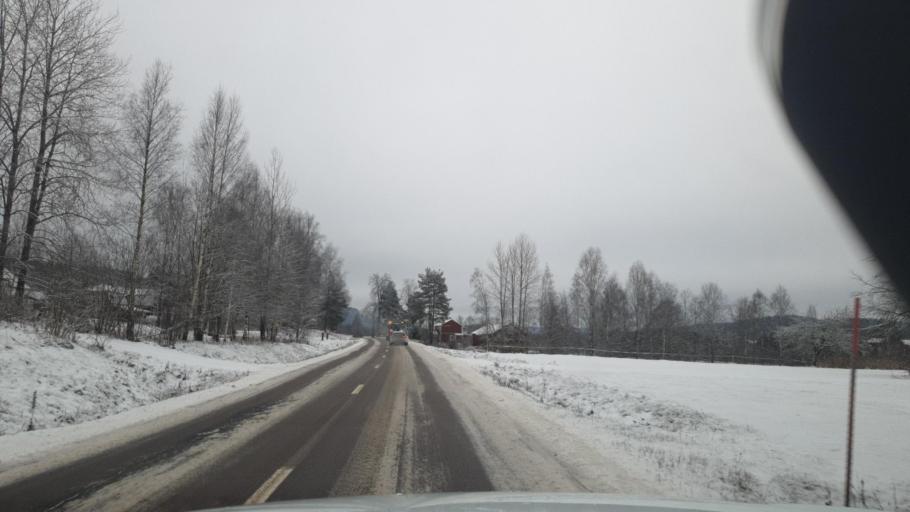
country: SE
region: Vaermland
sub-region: Eda Kommun
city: Amotfors
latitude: 59.6736
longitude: 12.1447
